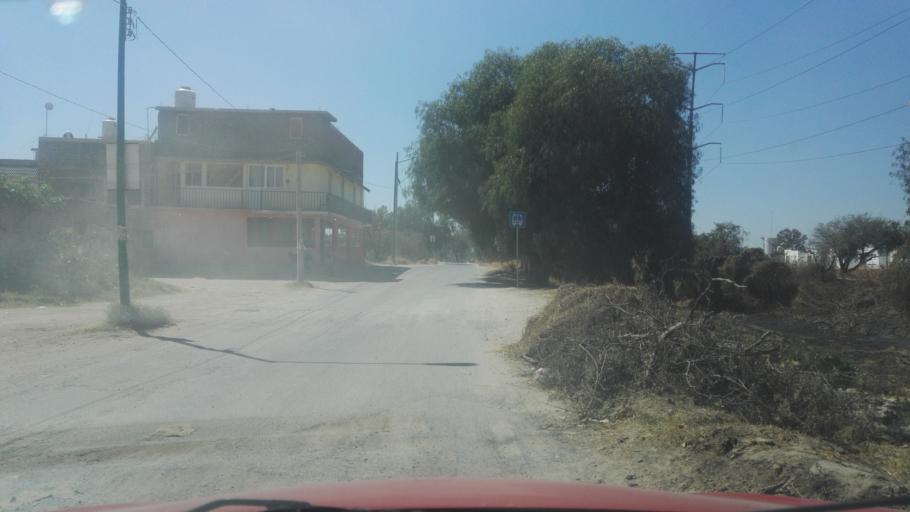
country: MX
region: Guanajuato
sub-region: Leon
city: Fraccionamiento Paraiso Real
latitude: 21.0821
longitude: -101.5956
